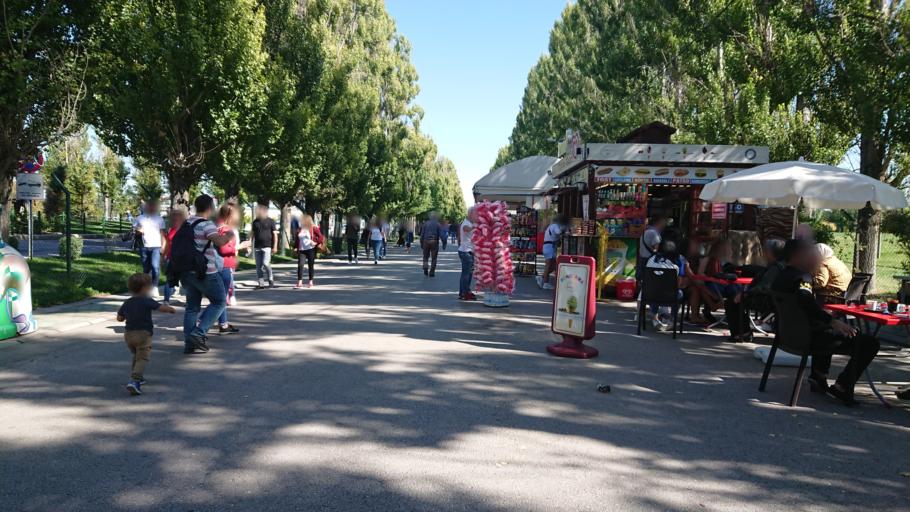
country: TR
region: Eskisehir
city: Eskisehir
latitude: 39.7648
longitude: 30.4731
